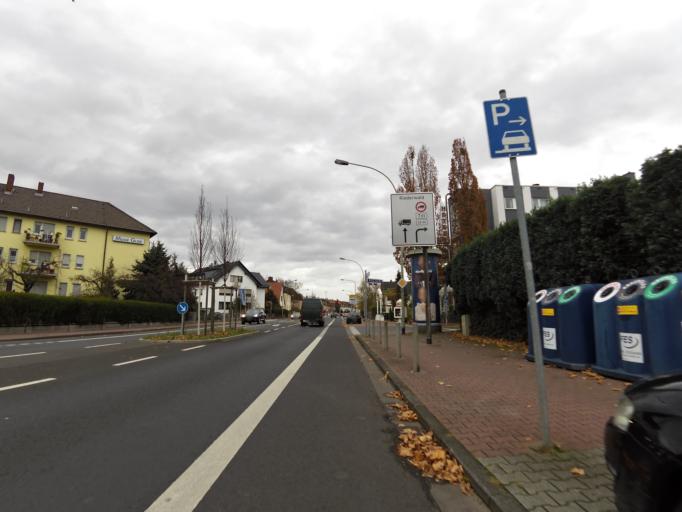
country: DE
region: Hesse
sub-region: Regierungsbezirk Darmstadt
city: Bad Vilbel
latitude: 50.1440
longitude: 8.7531
